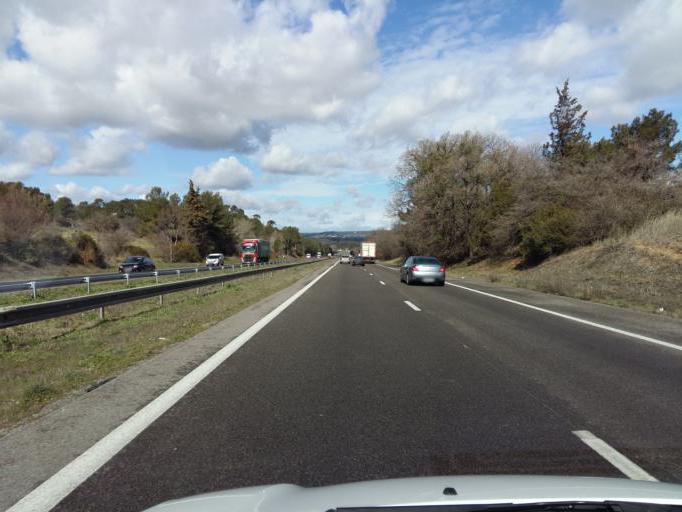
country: FR
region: Provence-Alpes-Cote d'Azur
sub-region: Departement des Bouches-du-Rhone
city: Bouc-Bel-Air
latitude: 43.4834
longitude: 5.4083
